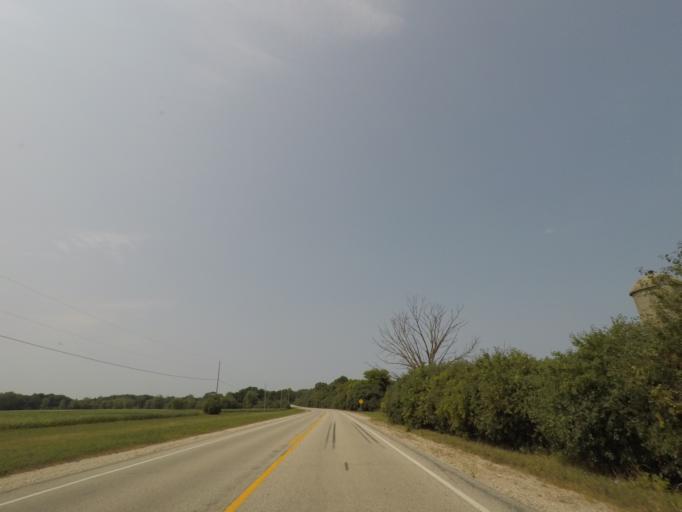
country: US
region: Wisconsin
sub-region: Waukesha County
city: Oconomowoc
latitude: 43.0623
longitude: -88.4888
